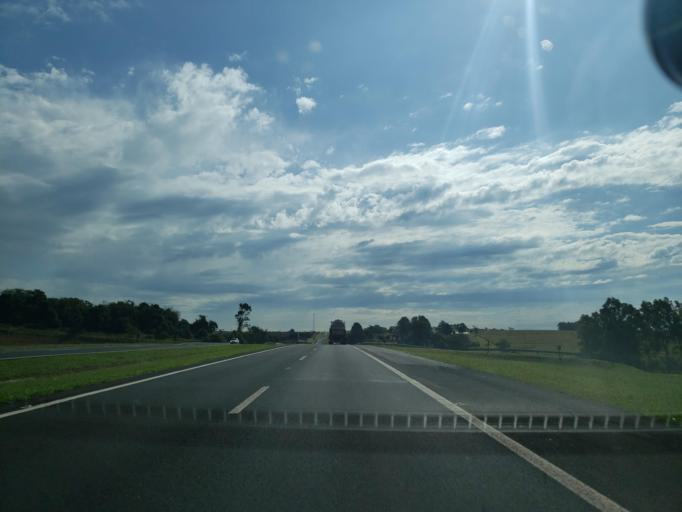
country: BR
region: Sao Paulo
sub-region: Cafelandia
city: Cafelandia
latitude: -21.8932
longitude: -49.5386
